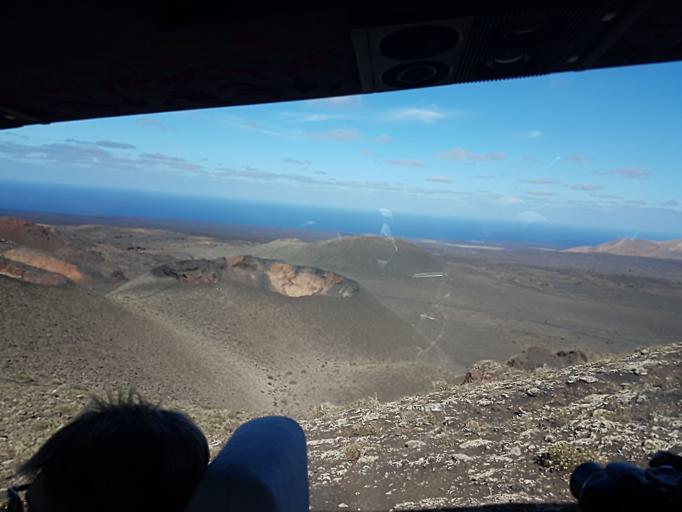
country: ES
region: Canary Islands
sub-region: Provincia de Las Palmas
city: Yaiza
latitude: 29.0032
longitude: -13.7481
